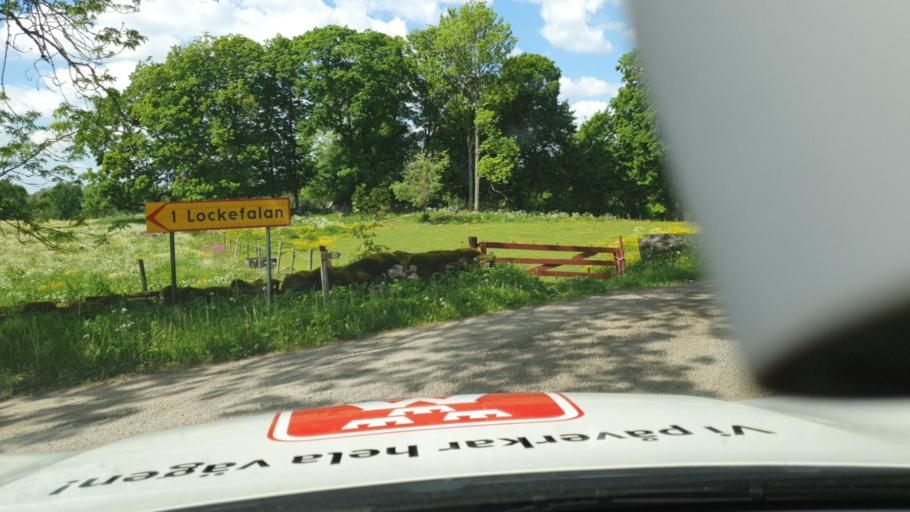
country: SE
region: Vaestra Goetaland
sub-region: Falkopings Kommun
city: Falkoeping
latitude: 58.0556
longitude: 13.6606
